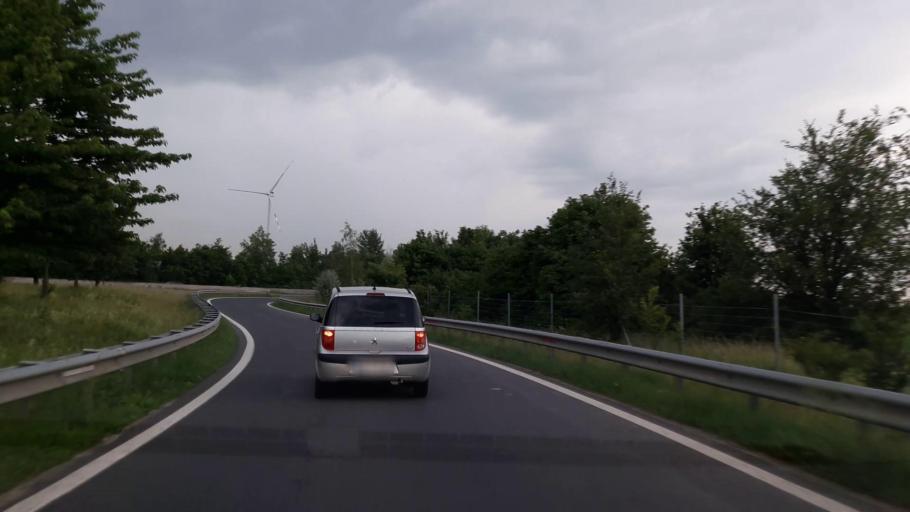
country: AT
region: Burgenland
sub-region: Politischer Bezirk Neusiedl am See
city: Parndorf
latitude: 48.0061
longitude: 16.8358
